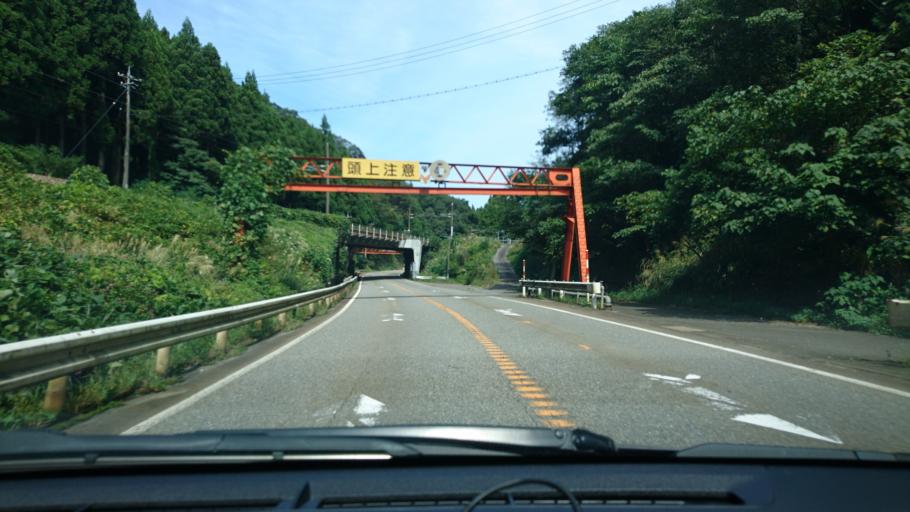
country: JP
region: Fukui
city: Maruoka
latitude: 36.2753
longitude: 136.2905
